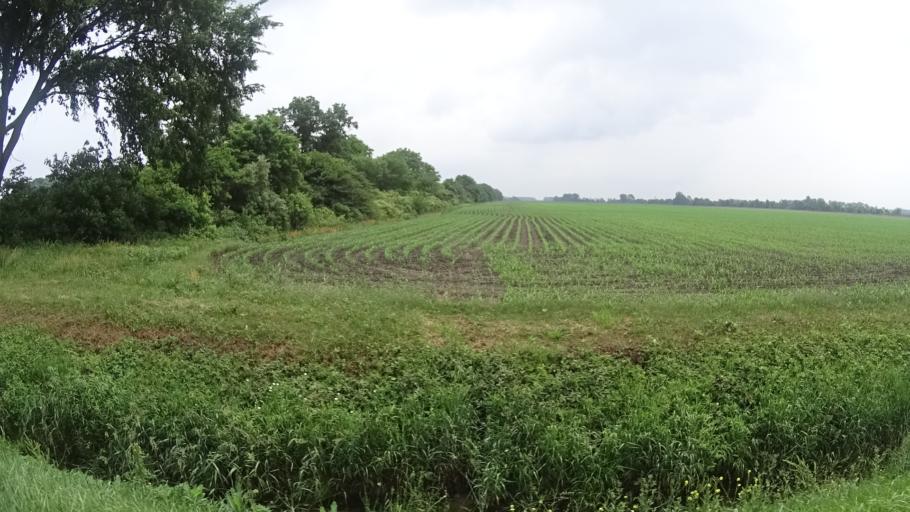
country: US
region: Ohio
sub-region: Huron County
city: Bellevue
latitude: 41.3189
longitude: -82.7930
